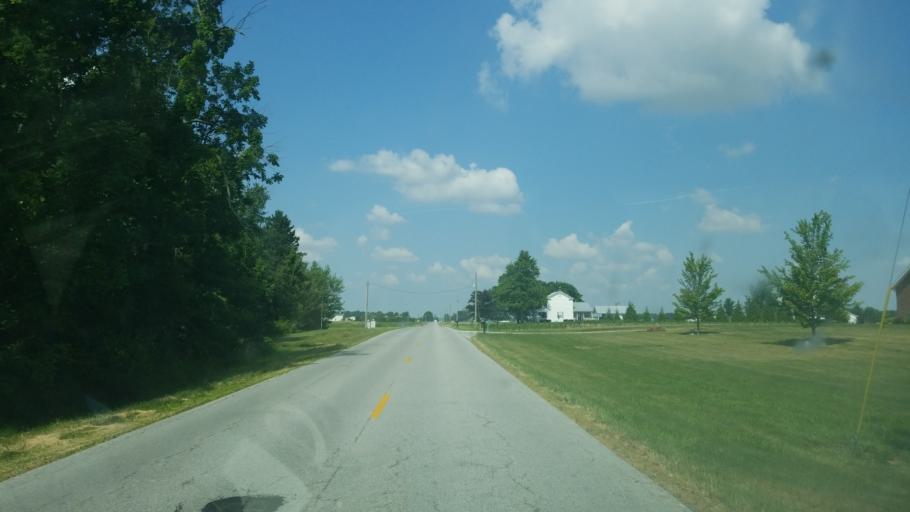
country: US
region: Ohio
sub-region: Auglaize County
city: Wapakoneta
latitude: 40.5703
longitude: -84.1359
